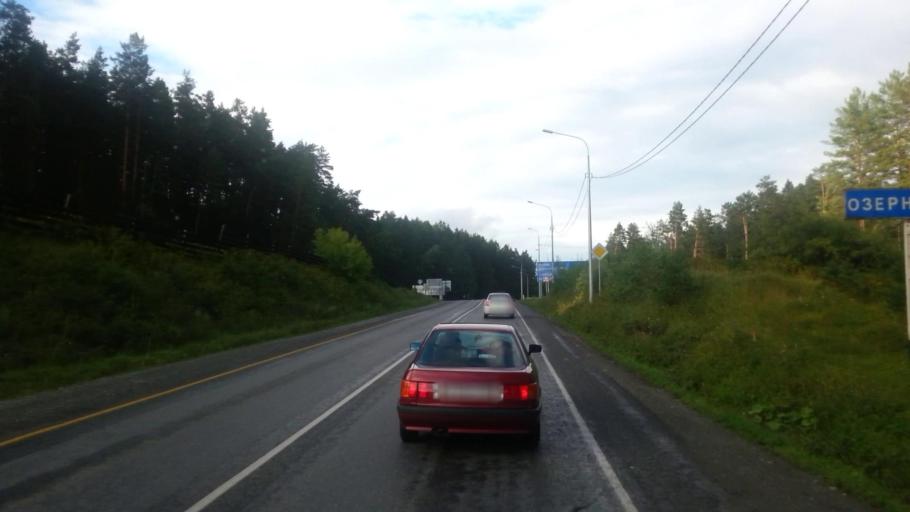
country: RU
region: Altay
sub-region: Mayminskiy Rayon
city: Manzherok
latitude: 51.8202
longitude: 85.7846
